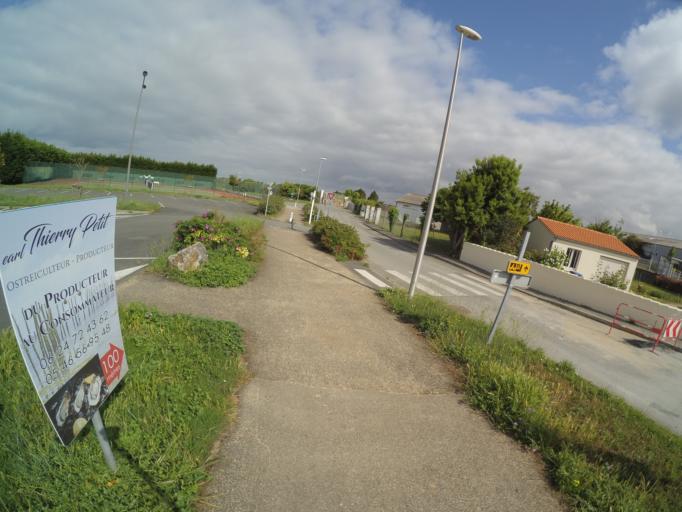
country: FR
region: Poitou-Charentes
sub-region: Departement de la Charente-Maritime
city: Angoulins
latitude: 46.1078
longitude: -1.1160
